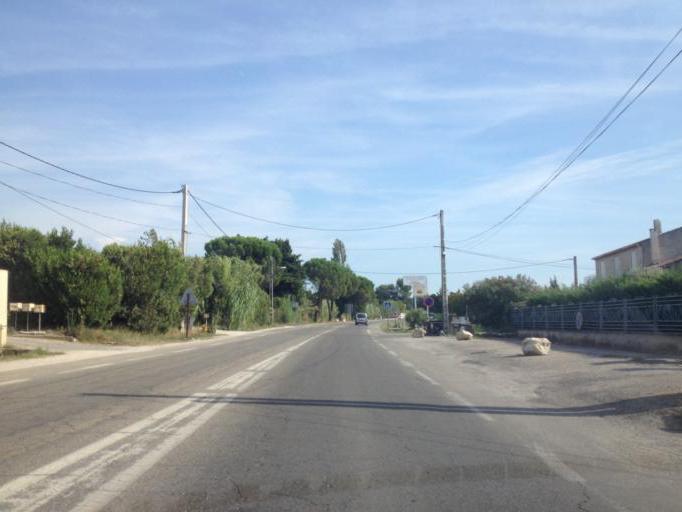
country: FR
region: Provence-Alpes-Cote d'Azur
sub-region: Departement du Vaucluse
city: Aubignan
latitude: 44.0902
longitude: 5.0313
